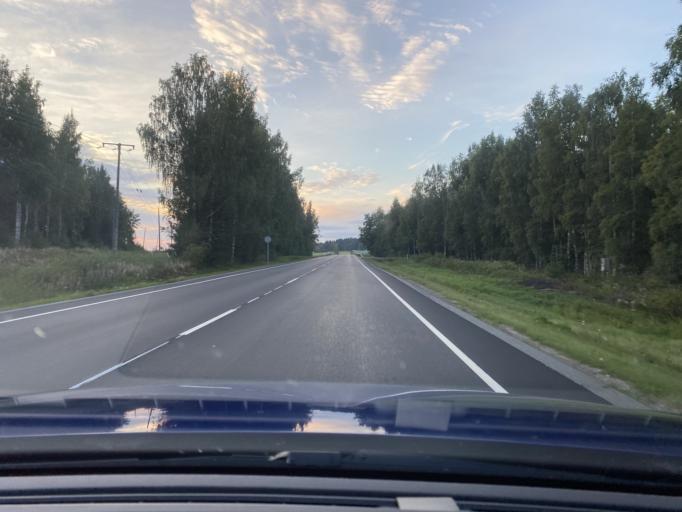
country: FI
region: Satakunta
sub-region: Pohjois-Satakunta
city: Kankaanpaeae
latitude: 61.8353
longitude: 22.3481
